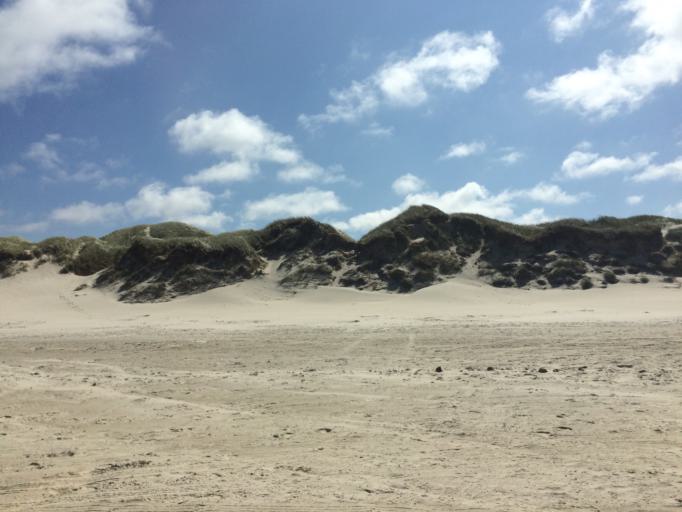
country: DK
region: North Denmark
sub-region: Jammerbugt Kommune
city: Pandrup
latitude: 57.2479
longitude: 9.5704
